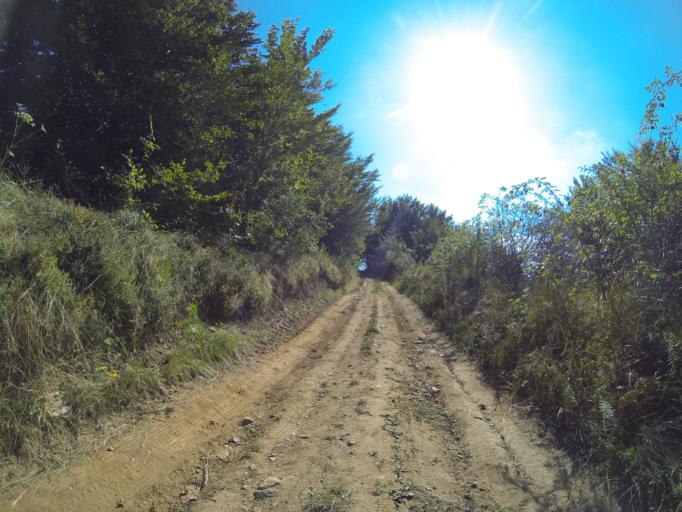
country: RO
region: Mehedinti
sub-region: Comuna Svinita
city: Svinita
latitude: 44.5653
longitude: 22.1385
